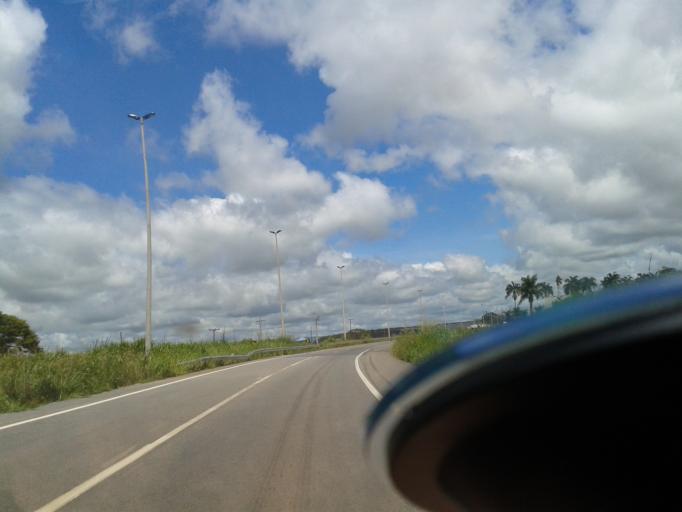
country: BR
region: Goias
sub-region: Itaberai
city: Itaberai
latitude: -16.0675
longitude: -49.7741
